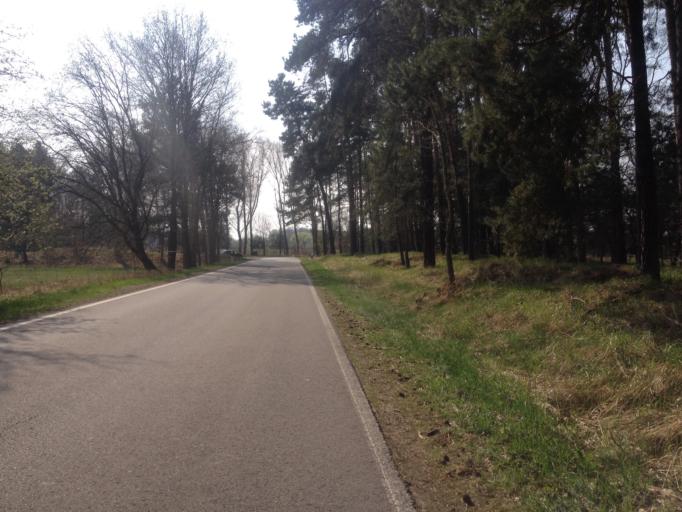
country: DE
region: Brandenburg
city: Drehnow
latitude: 51.8277
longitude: 14.3537
